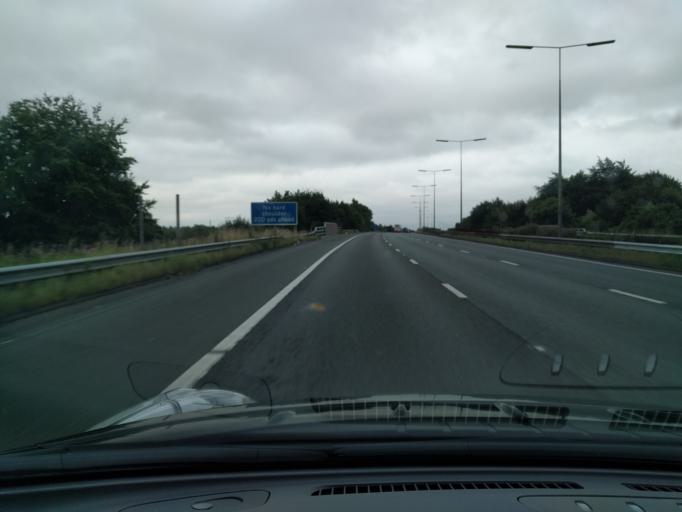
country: GB
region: England
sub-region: St. Helens
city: Newton-le-Willows
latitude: 53.4572
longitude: -2.6048
